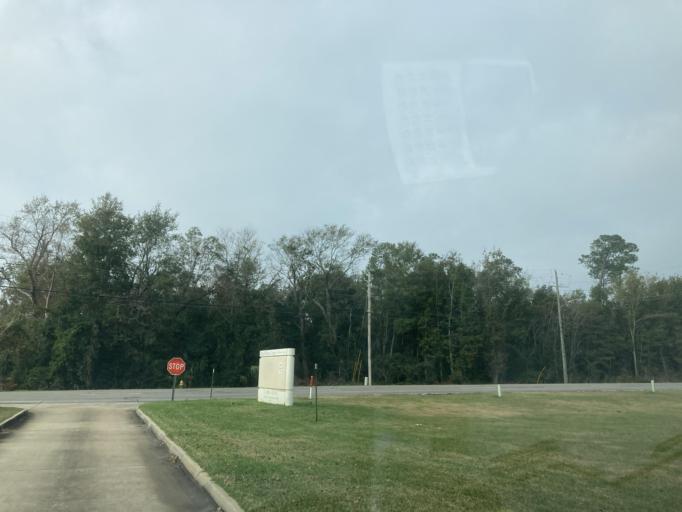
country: US
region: Mississippi
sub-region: Harrison County
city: Gulfport
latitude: 30.3691
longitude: -89.1184
